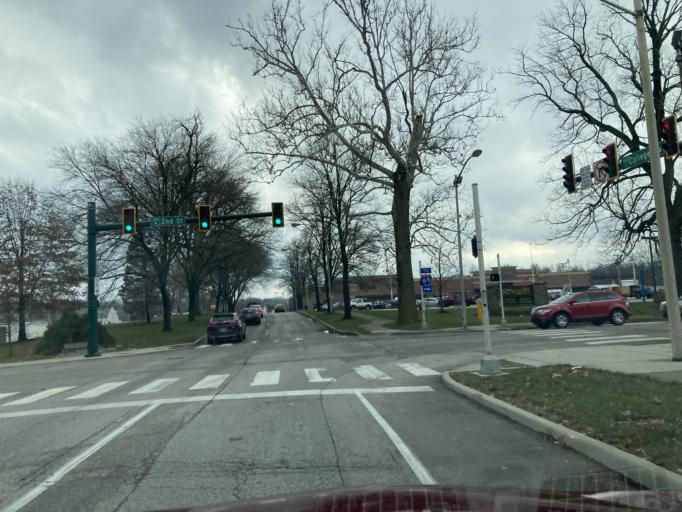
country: US
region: Indiana
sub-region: Monroe County
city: Bloomington
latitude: 39.1616
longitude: -86.5350
